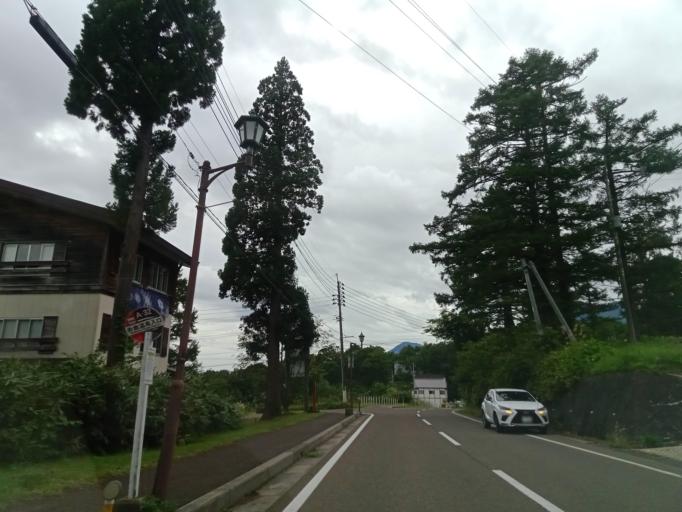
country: JP
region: Niigata
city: Arai
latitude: 36.8897
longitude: 138.1769
